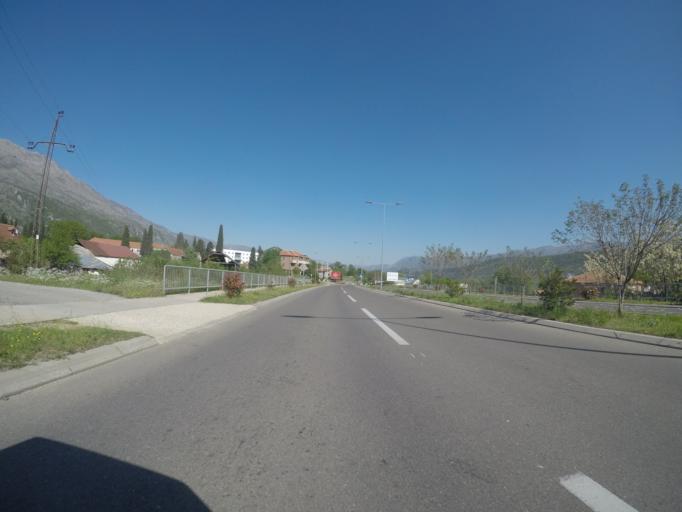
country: ME
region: Danilovgrad
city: Danilovgrad
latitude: 42.5529
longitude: 19.0898
